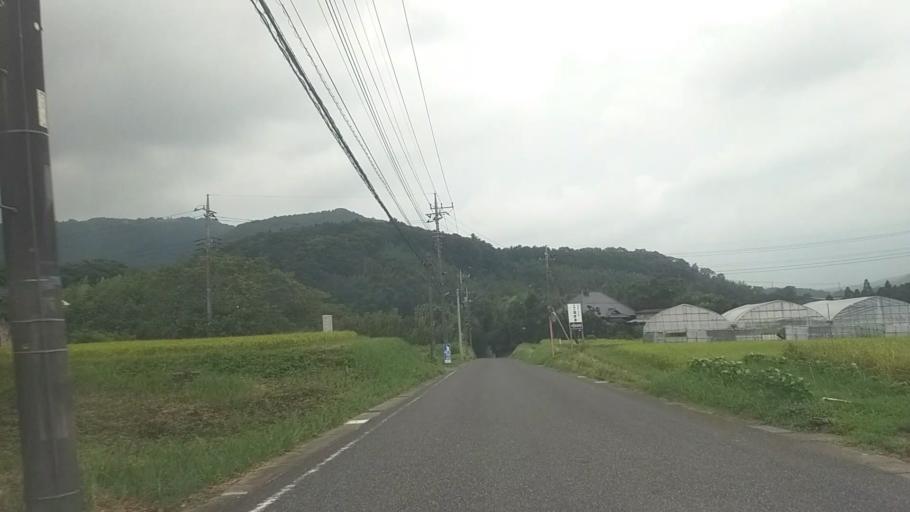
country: JP
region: Chiba
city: Kimitsu
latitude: 35.2463
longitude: 139.9928
